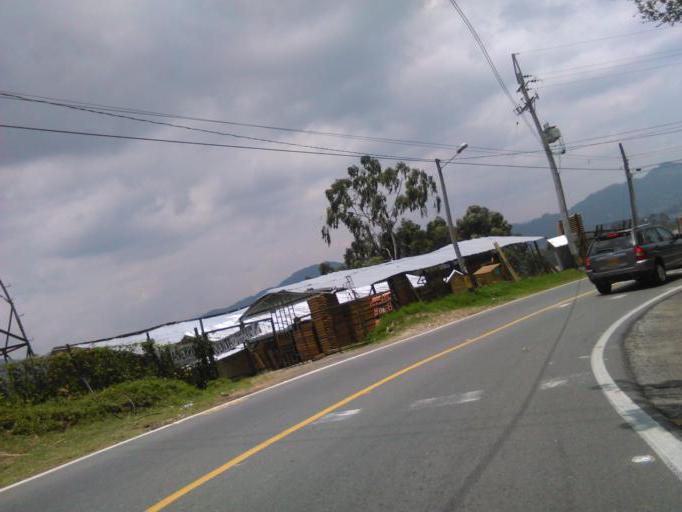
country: CO
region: Antioquia
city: La Ceja
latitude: 6.0169
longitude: -75.4061
